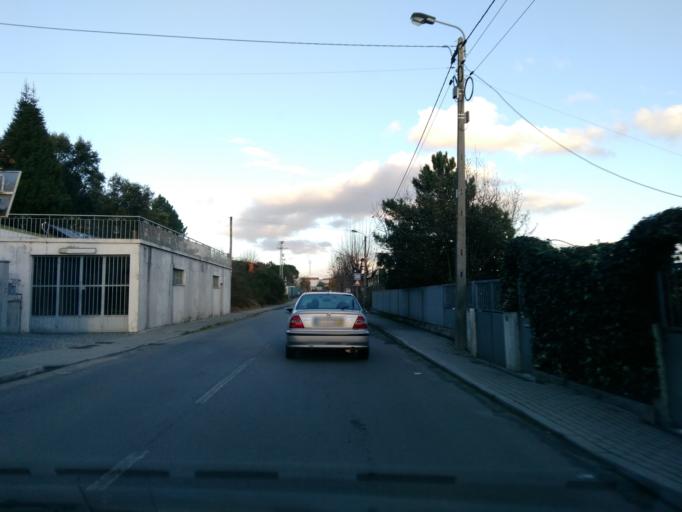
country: PT
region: Braga
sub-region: Braga
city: Braga
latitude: 41.5273
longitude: -8.4599
